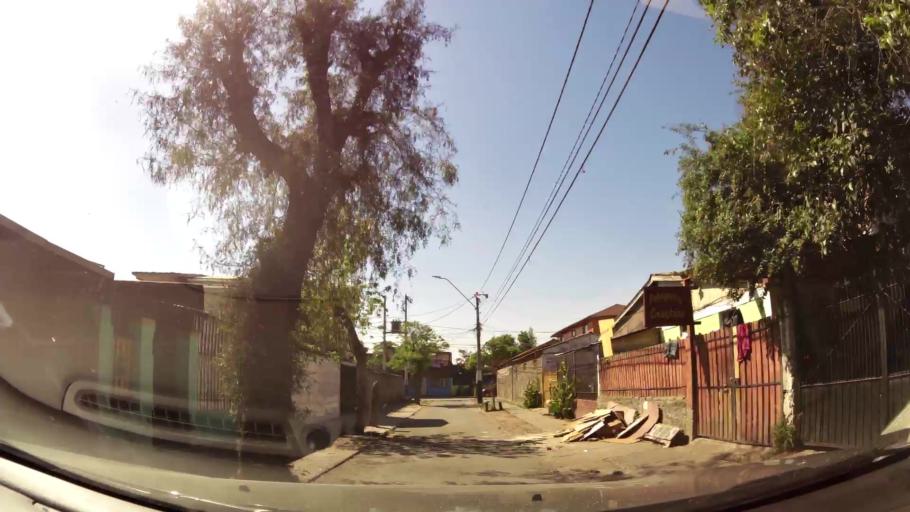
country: CL
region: Santiago Metropolitan
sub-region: Provincia de Maipo
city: San Bernardo
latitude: -33.5811
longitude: -70.7051
